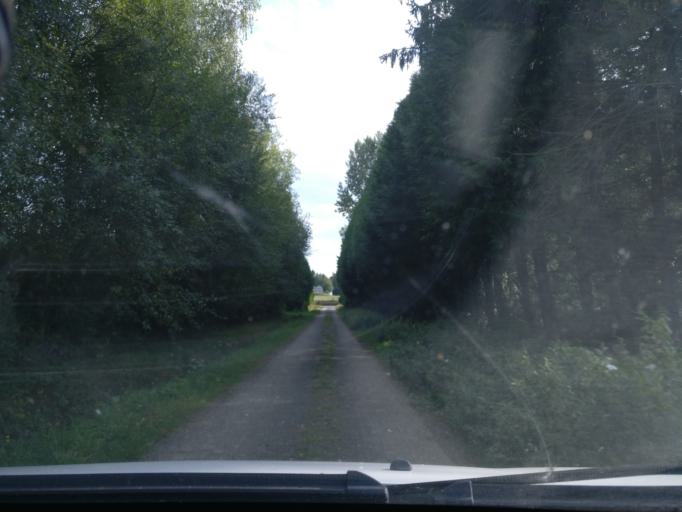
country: FR
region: Brittany
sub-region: Departement d'Ille-et-Vilaine
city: Fouillard
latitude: 48.1346
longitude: -1.5766
